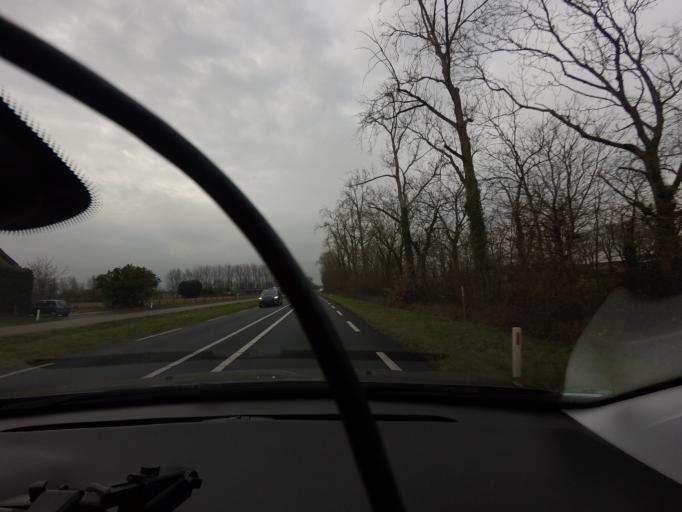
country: NL
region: North Holland
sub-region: Gemeente Hollands Kroon
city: Den Oever
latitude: 52.9051
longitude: 4.9660
